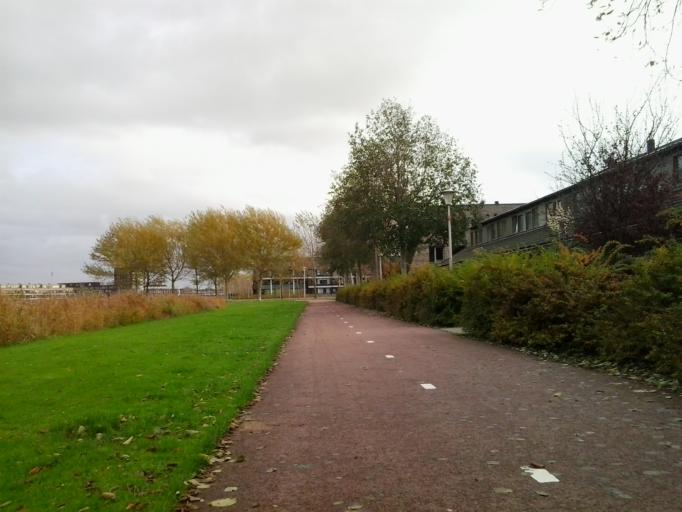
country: NL
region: South Holland
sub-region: Gemeente Lansingerland
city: Berkel en Rodenrijs
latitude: 51.9972
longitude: 4.4634
